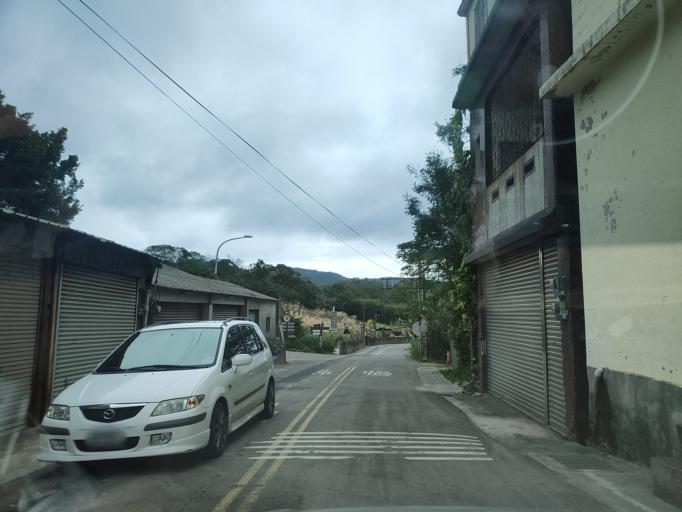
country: TW
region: Taiwan
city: Fengyuan
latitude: 24.3824
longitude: 120.7588
